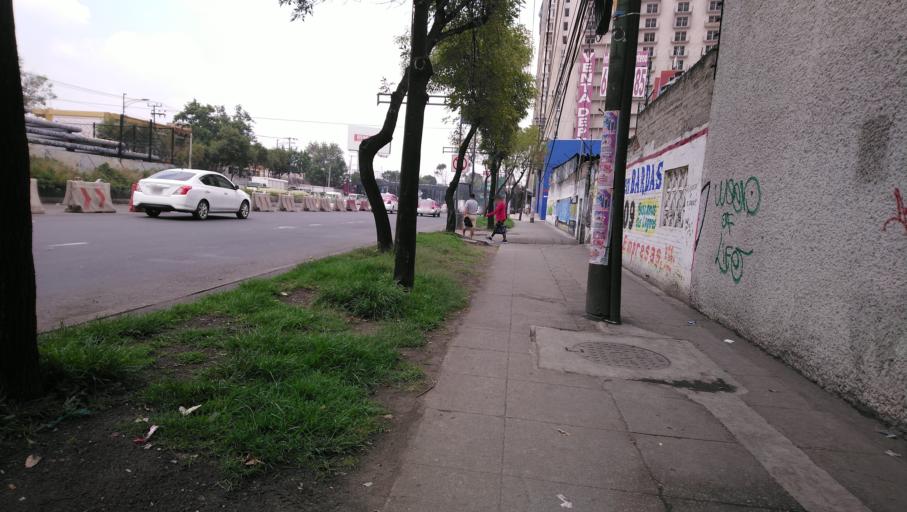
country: MX
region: Mexico City
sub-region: Iztacalco
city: Iztacalco
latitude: 19.4002
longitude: -99.1134
